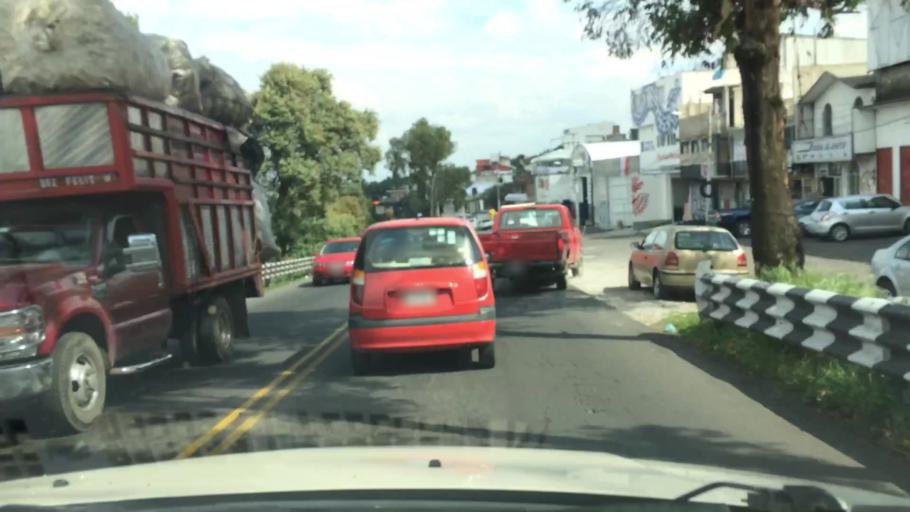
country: MX
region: Mexico City
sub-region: Tlalpan
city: Lomas de Tepemecatl
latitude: 19.2682
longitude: -99.2128
